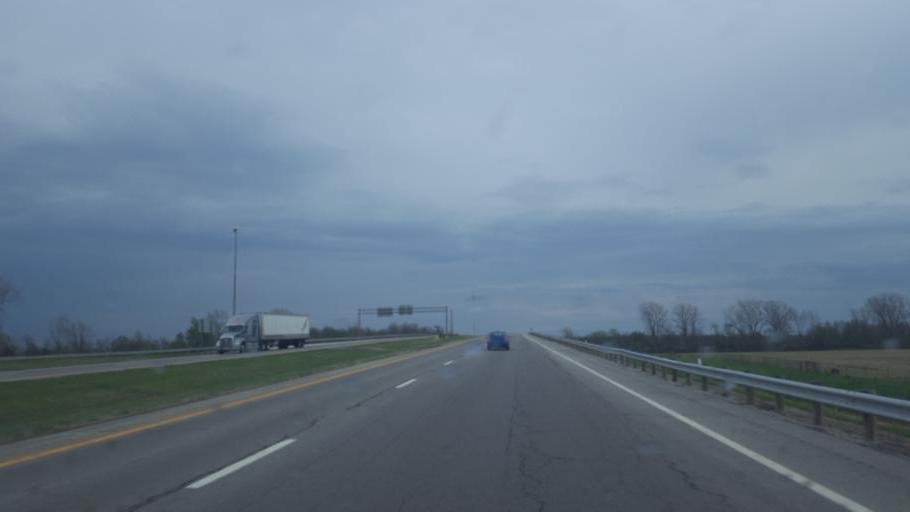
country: US
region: Ohio
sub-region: Wyandot County
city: Carey
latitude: 40.9398
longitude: -83.3988
